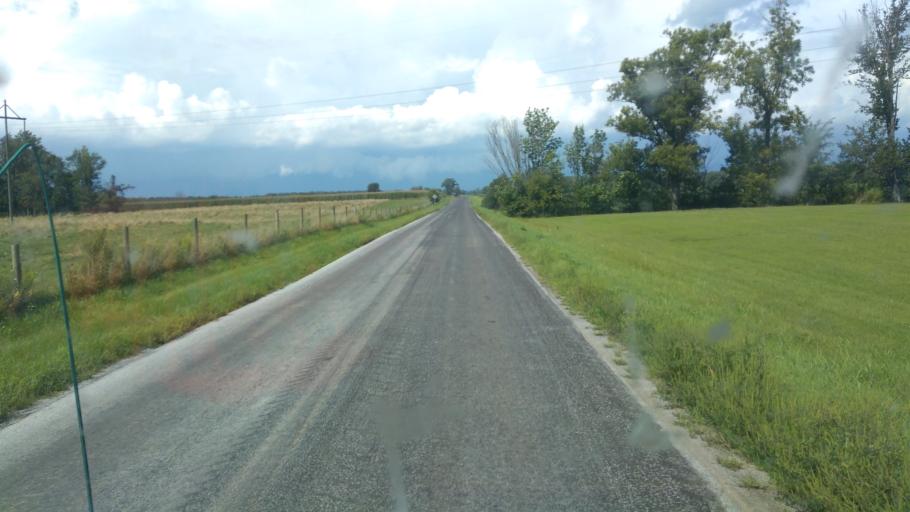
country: US
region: Ohio
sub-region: Hardin County
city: Kenton
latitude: 40.5893
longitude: -83.4630
